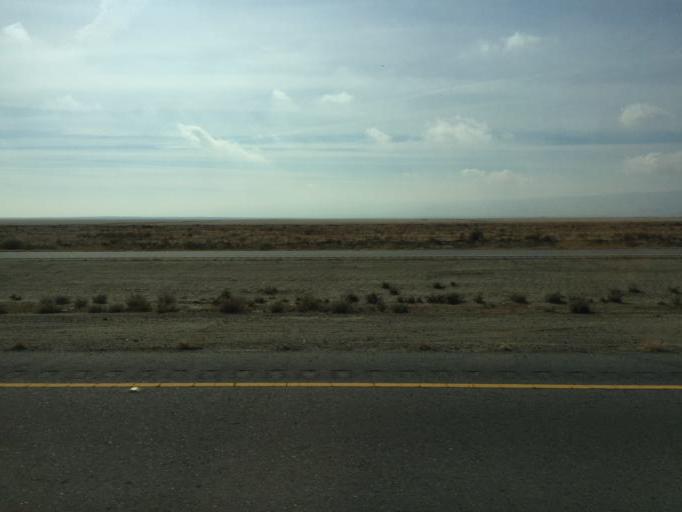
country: US
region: California
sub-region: Kern County
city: Lost Hills
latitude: 35.6149
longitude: -119.8892
